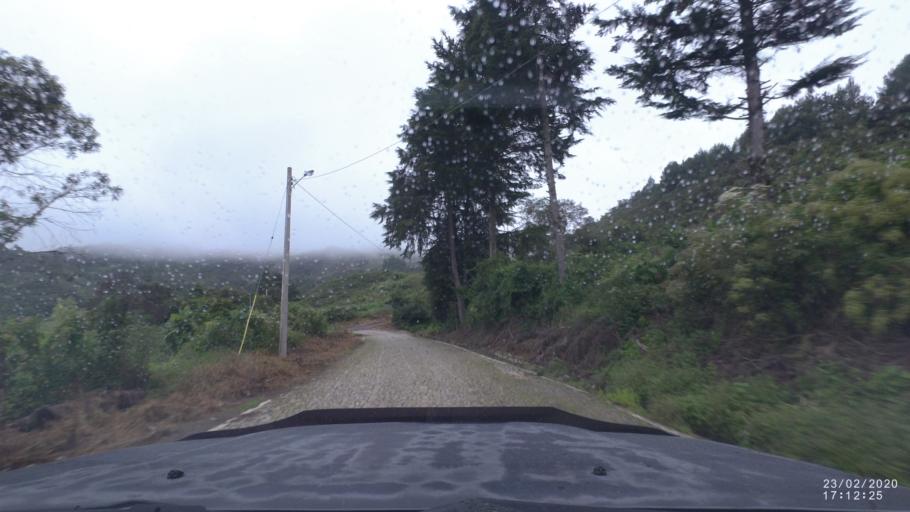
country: BO
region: Cochabamba
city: Colomi
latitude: -17.1346
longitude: -65.9432
